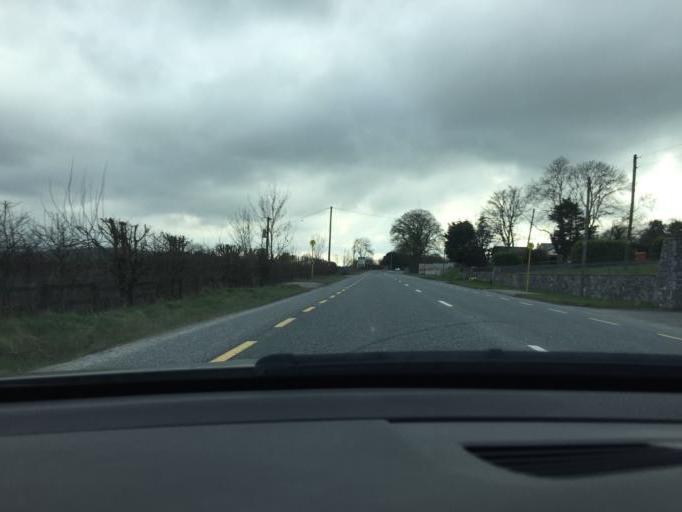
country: IE
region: Leinster
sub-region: South Dublin
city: Rathcoole
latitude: 53.2177
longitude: -6.4730
